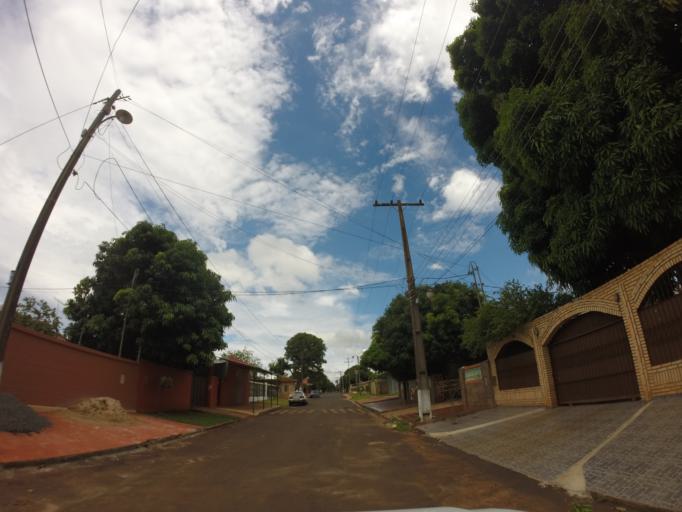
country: PY
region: Alto Parana
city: Ciudad del Este
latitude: -25.4143
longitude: -54.6271
